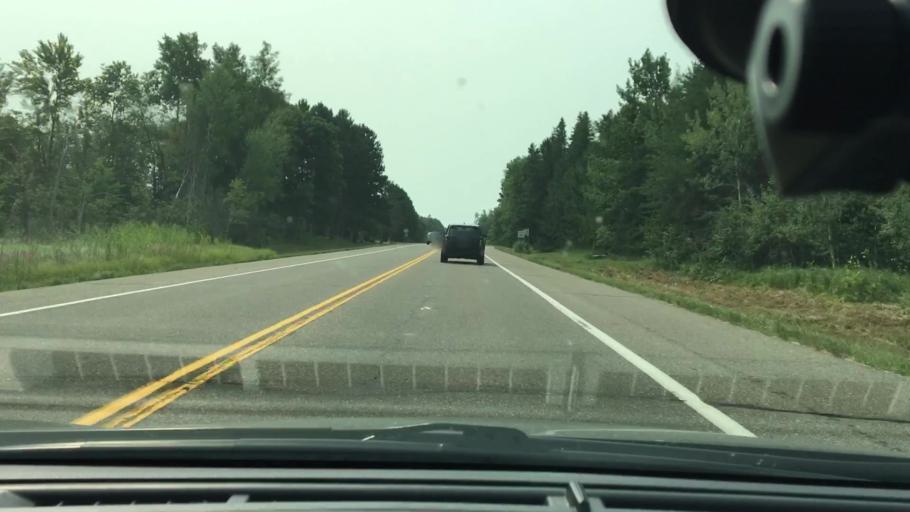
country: US
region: Minnesota
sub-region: Crow Wing County
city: Brainerd
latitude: 46.3959
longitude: -94.2234
